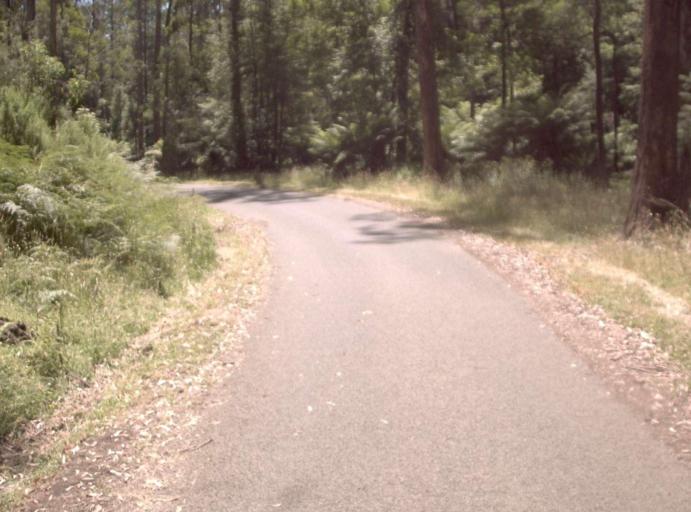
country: AU
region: Victoria
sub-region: Yarra Ranges
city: Millgrove
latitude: -37.6377
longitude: 145.7187
